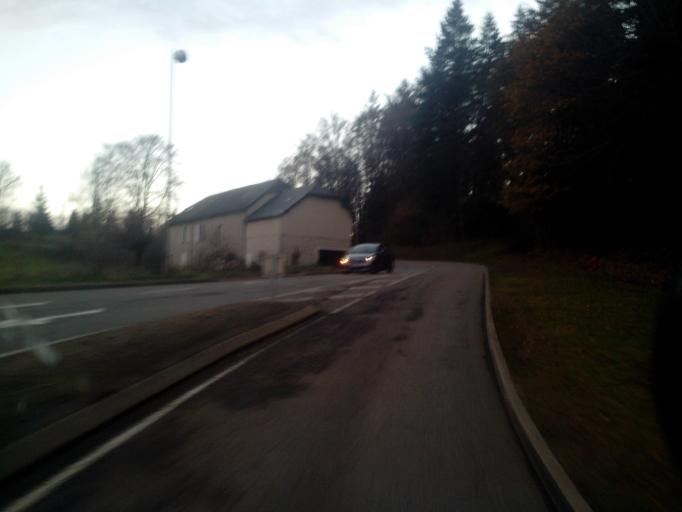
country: FR
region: Limousin
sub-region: Departement de la Correze
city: Meymac
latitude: 45.5309
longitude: 2.1557
